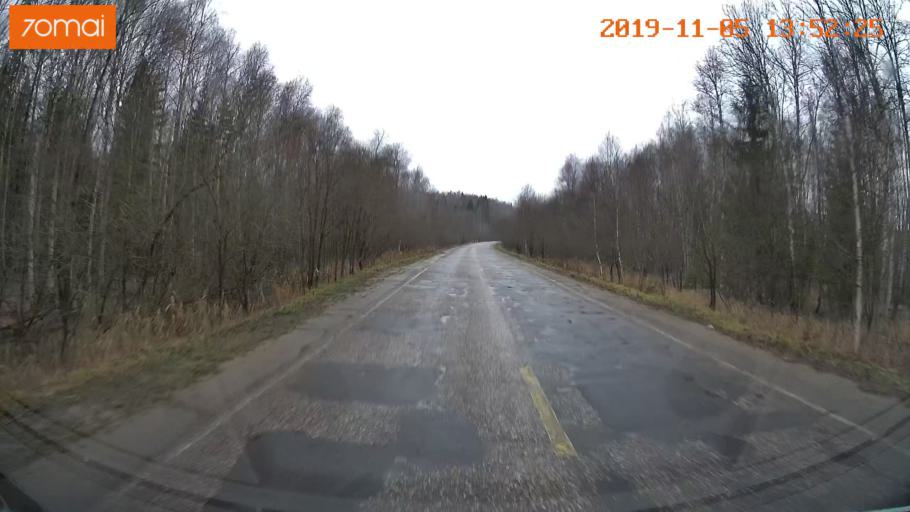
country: RU
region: Ivanovo
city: Kaminskiy
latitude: 57.0275
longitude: 41.3862
